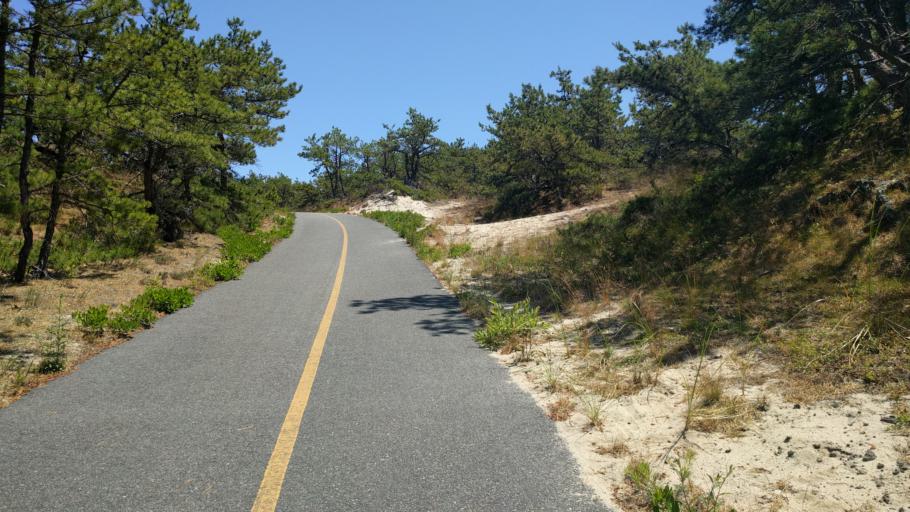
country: US
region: Massachusetts
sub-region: Barnstable County
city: Provincetown
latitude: 42.0605
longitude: -70.2143
